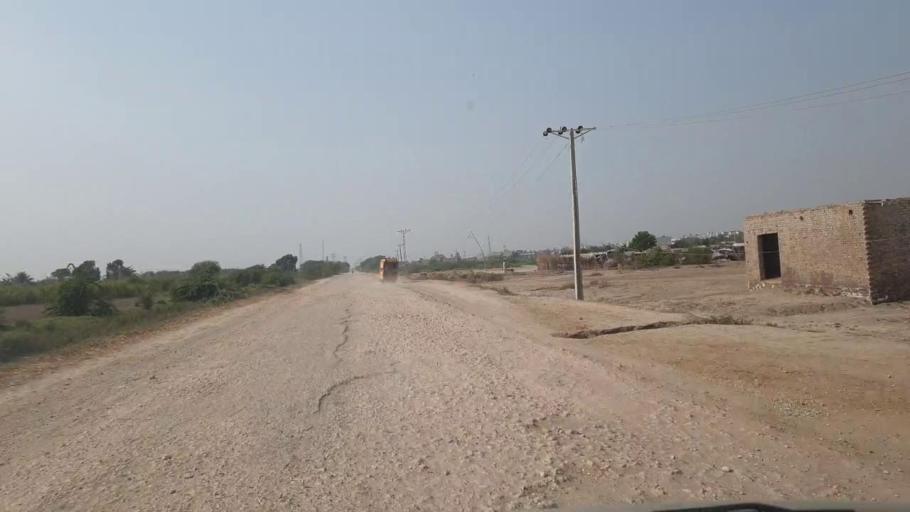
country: PK
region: Sindh
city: Matli
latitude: 25.0308
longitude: 68.6639
